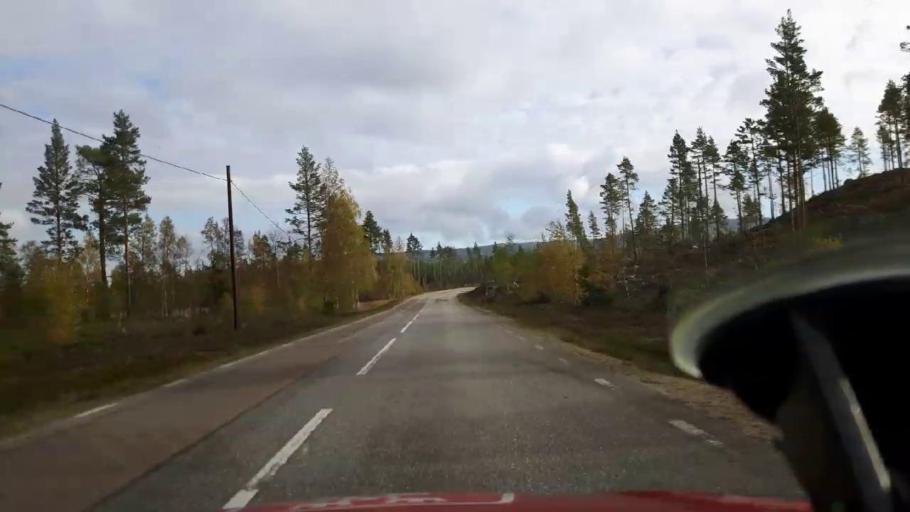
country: SE
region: Jaemtland
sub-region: Harjedalens Kommun
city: Sveg
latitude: 62.1244
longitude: 15.0188
